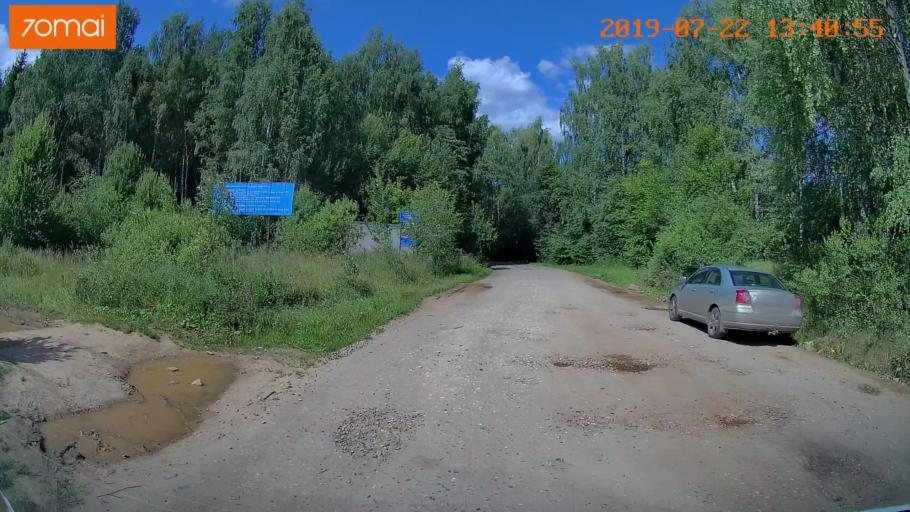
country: RU
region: Ivanovo
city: Novo-Talitsy
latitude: 57.0781
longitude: 40.8804
